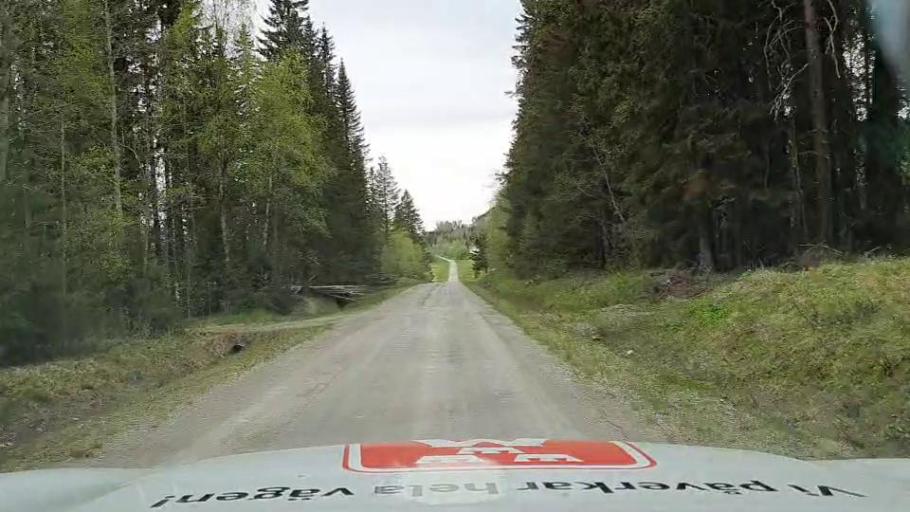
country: SE
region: Jaemtland
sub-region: Bergs Kommun
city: Hoverberg
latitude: 62.6645
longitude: 14.8239
